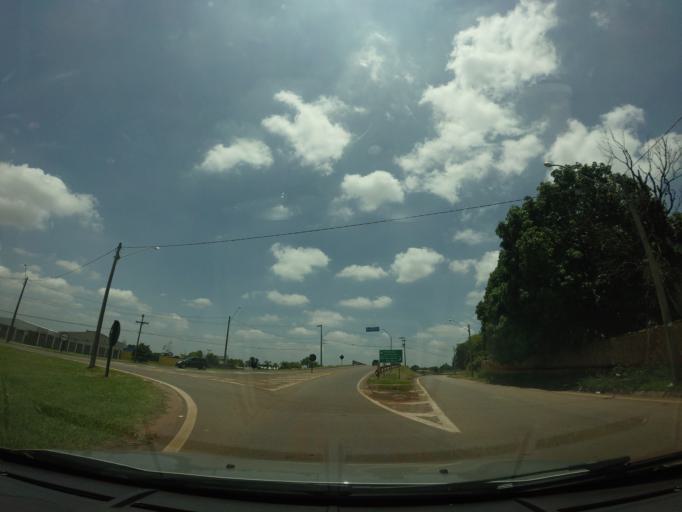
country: BR
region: Sao Paulo
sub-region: Piracicaba
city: Piracicaba
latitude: -22.7637
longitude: -47.5966
